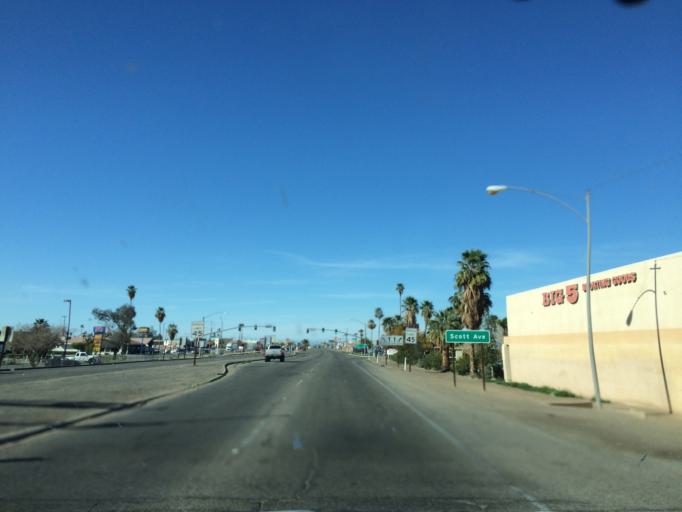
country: US
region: California
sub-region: Imperial County
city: El Centro
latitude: 32.7999
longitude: -115.5699
